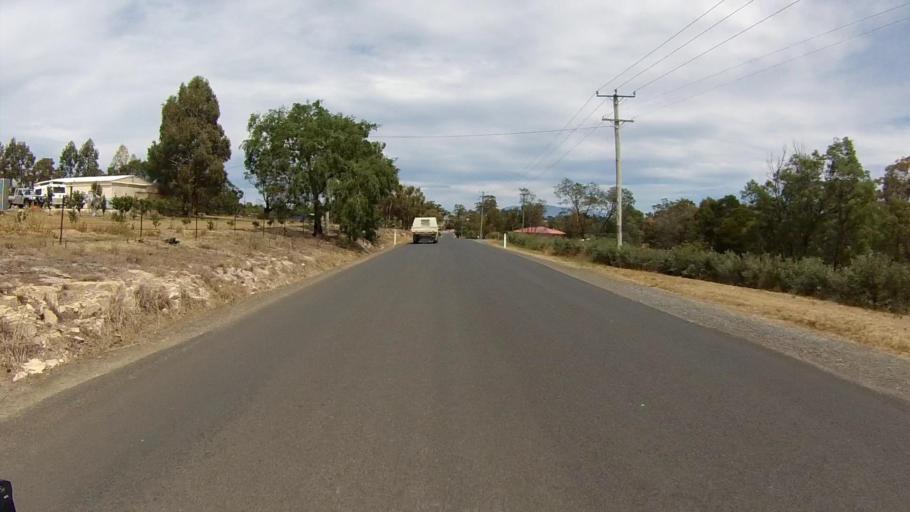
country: AU
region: Tasmania
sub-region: Sorell
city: Sorell
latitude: -42.8058
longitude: 147.6388
